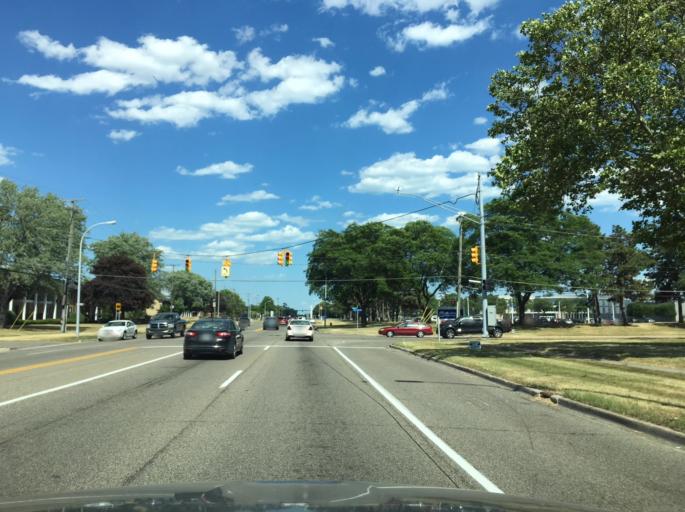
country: US
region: Michigan
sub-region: Macomb County
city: Fraser
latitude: 42.5082
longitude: -82.9785
